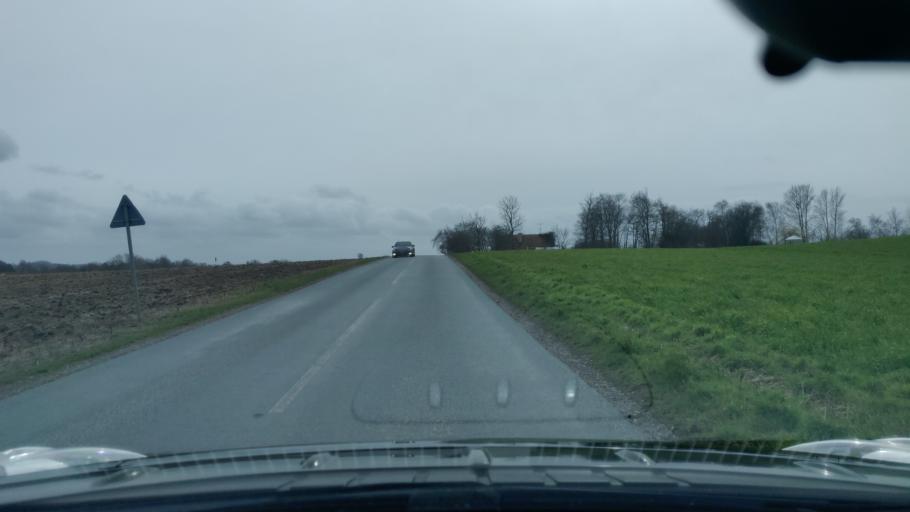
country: DK
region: Zealand
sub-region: Odsherred Kommune
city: Hojby
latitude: 55.9163
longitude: 11.5943
